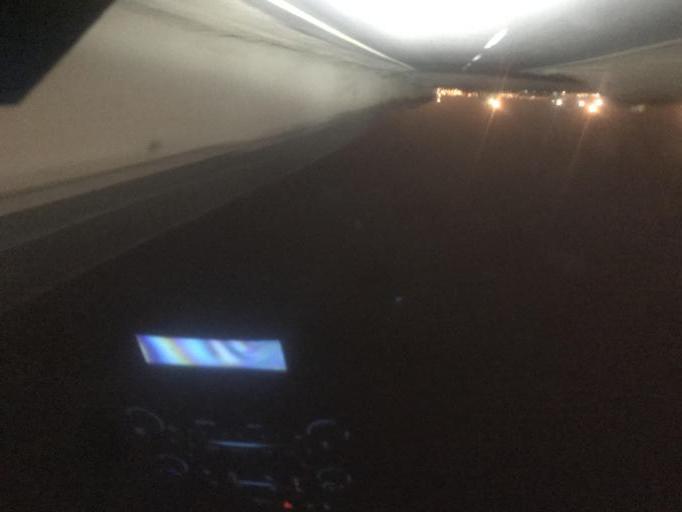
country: SA
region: Ar Riyad
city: Riyadh
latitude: 24.7635
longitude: 46.5870
